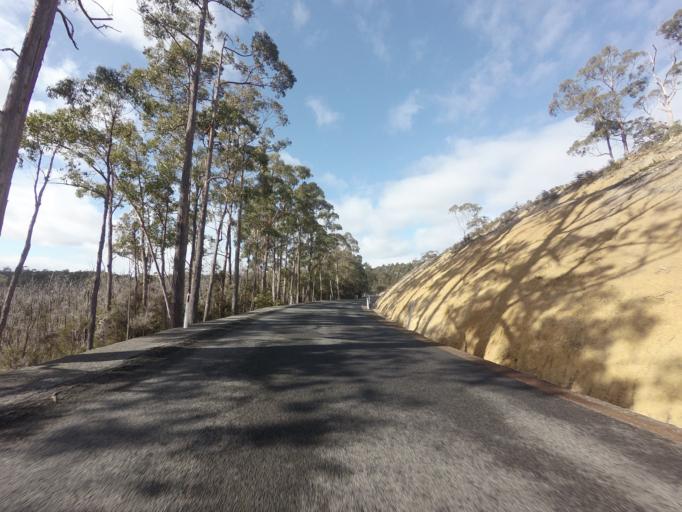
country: AU
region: Tasmania
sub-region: Huon Valley
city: Geeveston
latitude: -43.4250
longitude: 146.9055
